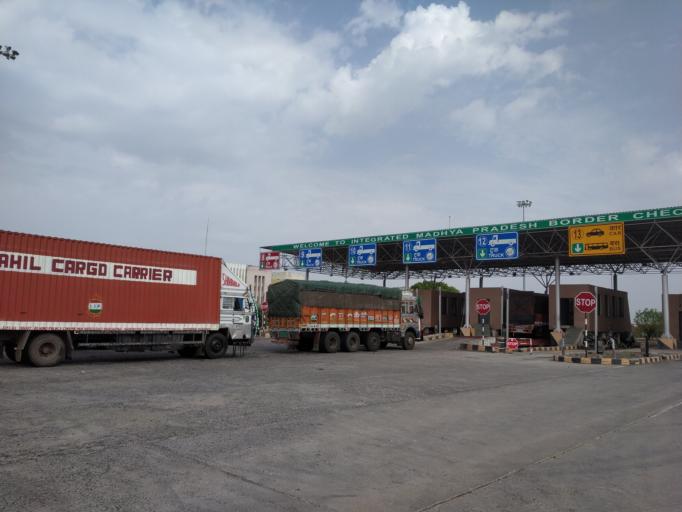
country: IN
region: Rajasthan
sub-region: Jhalawar
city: Bakani
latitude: 24.2563
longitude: 76.1598
